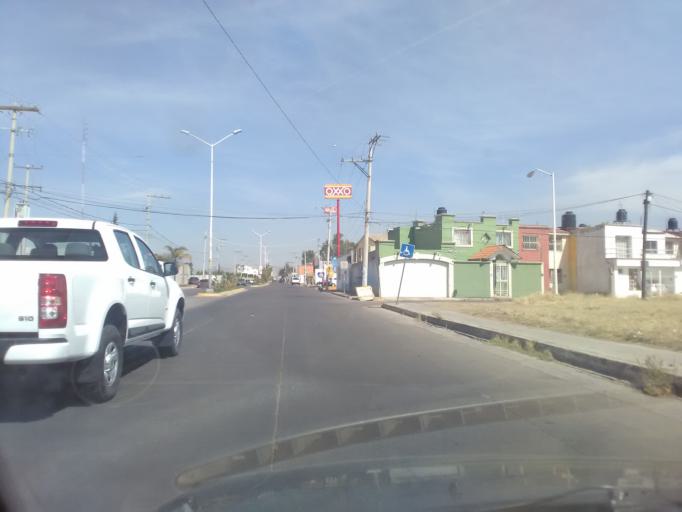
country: MX
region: Durango
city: Victoria de Durango
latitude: 24.0492
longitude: -104.6251
